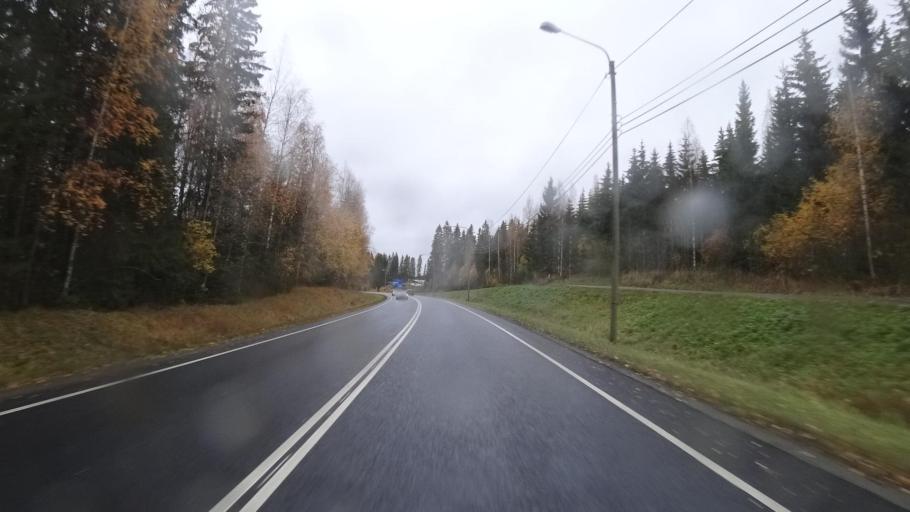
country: FI
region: Northern Savo
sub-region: Kuopio
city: Kuopio
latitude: 62.9830
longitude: 27.7878
